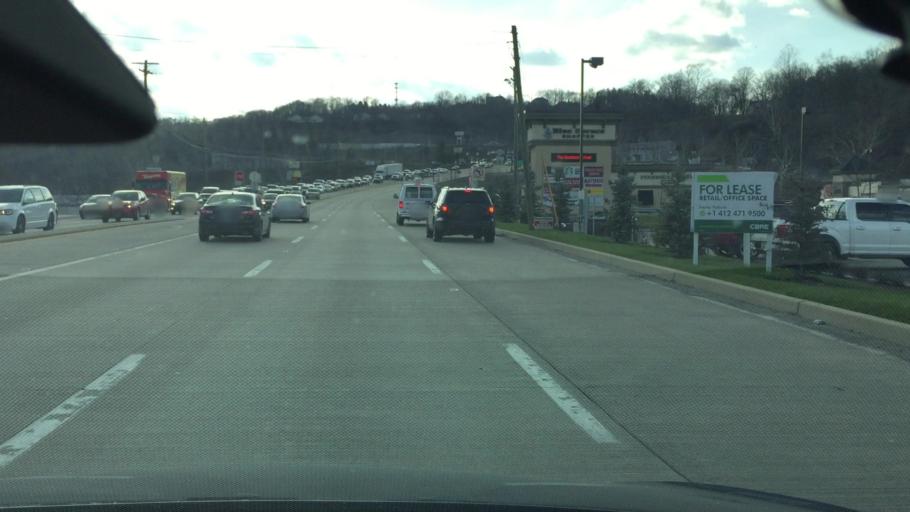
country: US
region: Pennsylvania
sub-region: Westmoreland County
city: Murrysville
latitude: 40.4271
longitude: -79.7001
